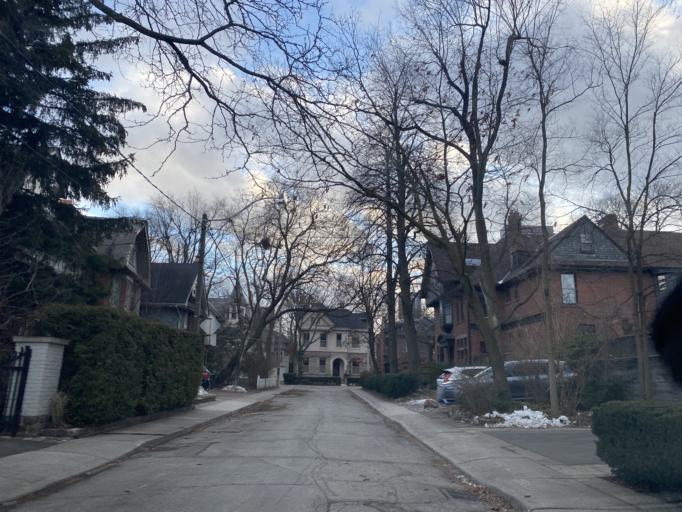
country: CA
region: Ontario
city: Toronto
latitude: 43.6763
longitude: -79.3765
